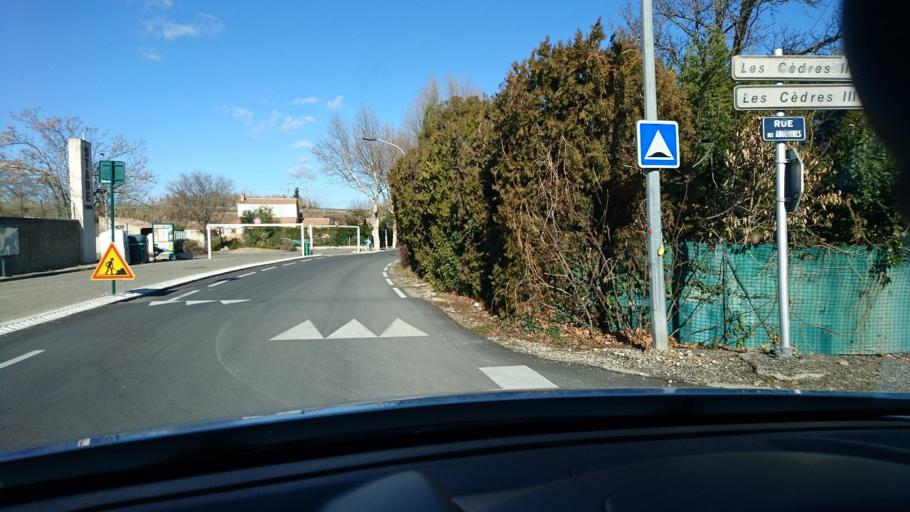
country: FR
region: Provence-Alpes-Cote d'Azur
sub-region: Departement du Vaucluse
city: Morieres-les-Avignon
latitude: 43.9345
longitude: 4.9054
